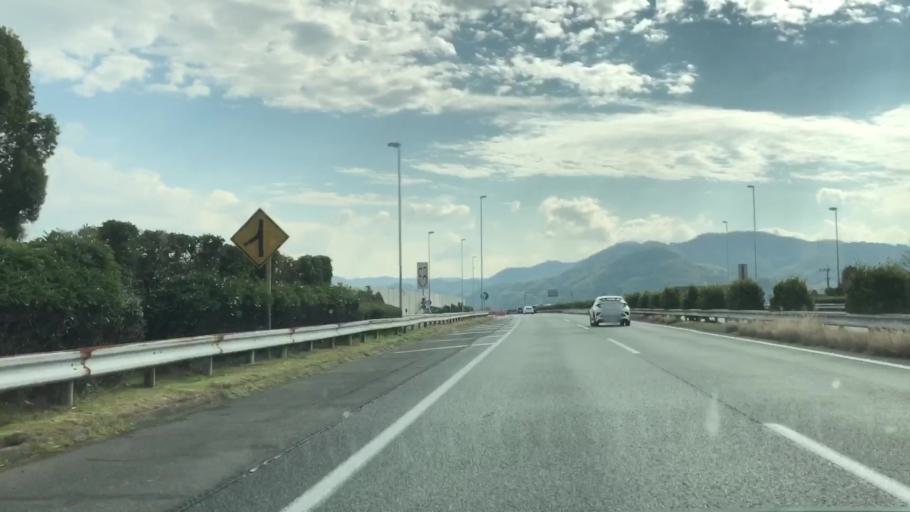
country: JP
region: Fukuoka
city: Setakamachi-takayanagi
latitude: 33.1279
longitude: 130.5179
